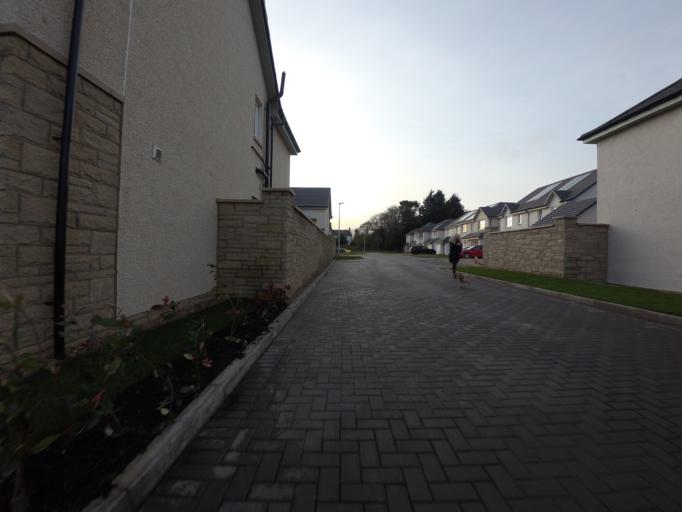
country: GB
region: Scotland
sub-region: West Lothian
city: Mid Calder
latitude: 55.9128
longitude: -3.4962
